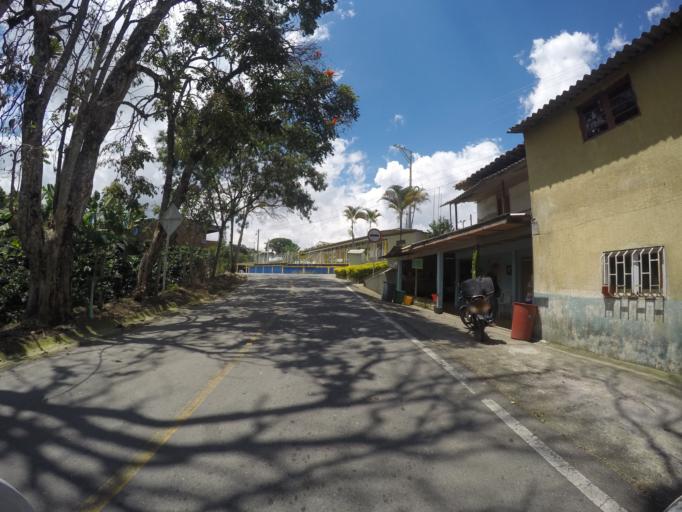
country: CO
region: Quindio
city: Quimbaya
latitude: 4.6299
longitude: -75.7184
